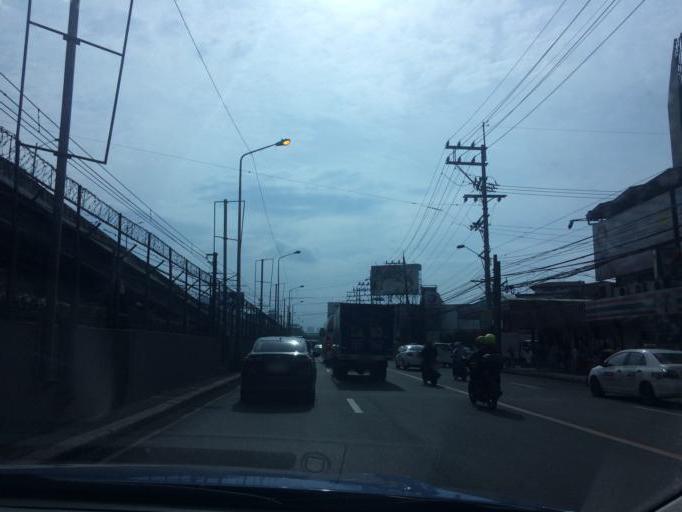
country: PH
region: Metro Manila
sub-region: Makati City
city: Makati City
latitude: 14.5380
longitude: 121.0056
